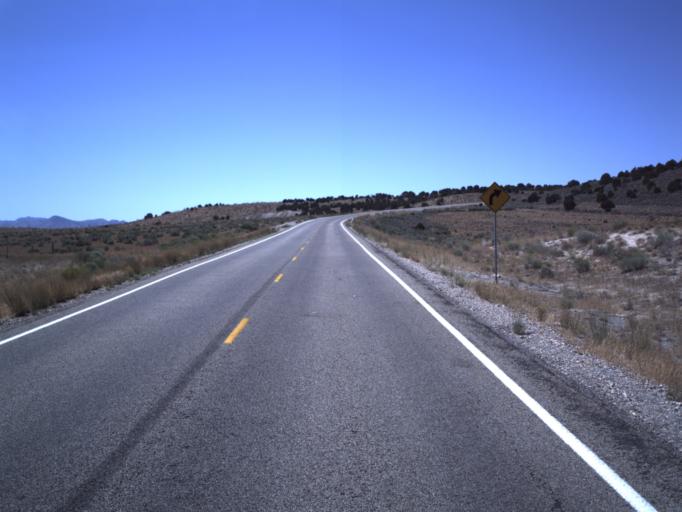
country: US
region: Utah
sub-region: Juab County
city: Nephi
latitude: 39.6684
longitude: -112.0337
